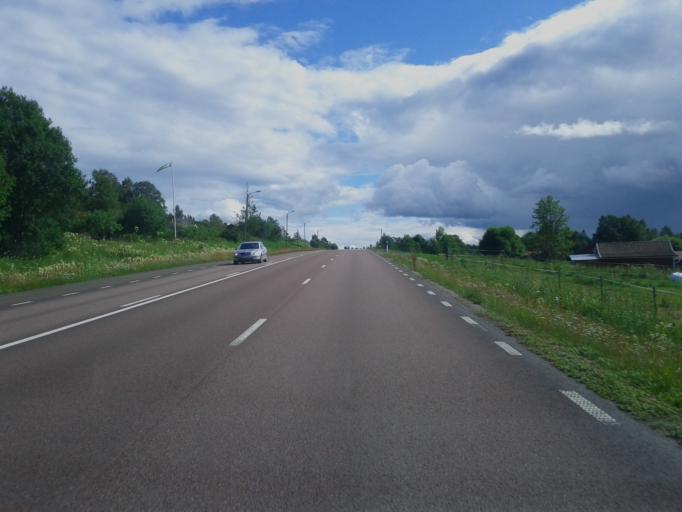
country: SE
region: Dalarna
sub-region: Rattviks Kommun
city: Raettvik
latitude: 60.8571
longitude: 15.1081
